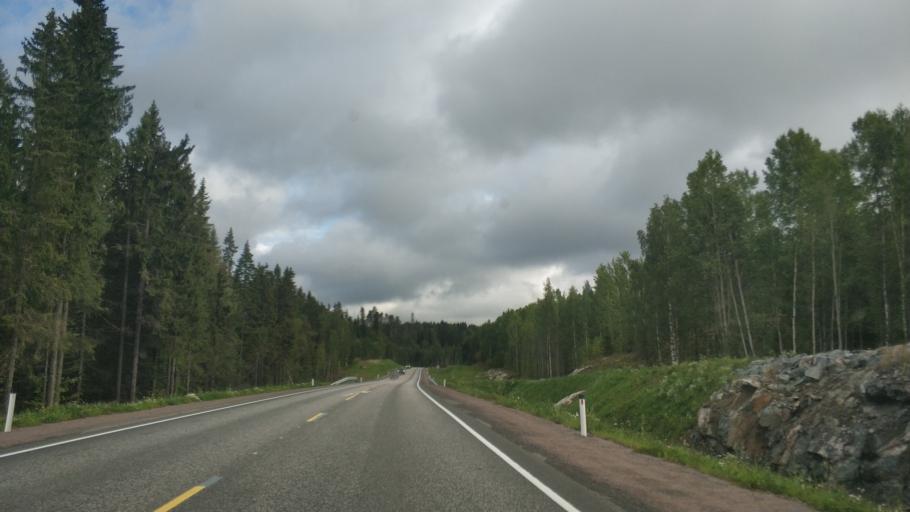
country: RU
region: Republic of Karelia
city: Khelyulya
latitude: 61.8070
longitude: 30.6207
